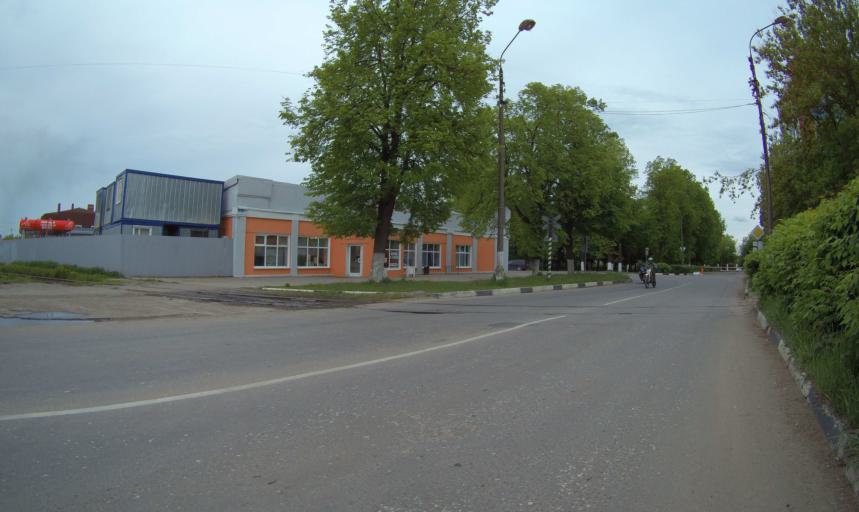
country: RU
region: Moskovskaya
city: Kolomna
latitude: 55.0711
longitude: 38.8033
